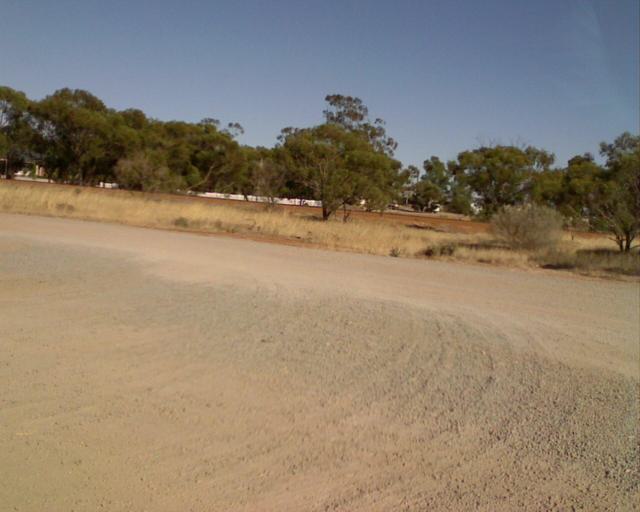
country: AU
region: Western Australia
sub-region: Wongan-Ballidu
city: Wongan Hills
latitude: -30.2730
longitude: 116.6656
